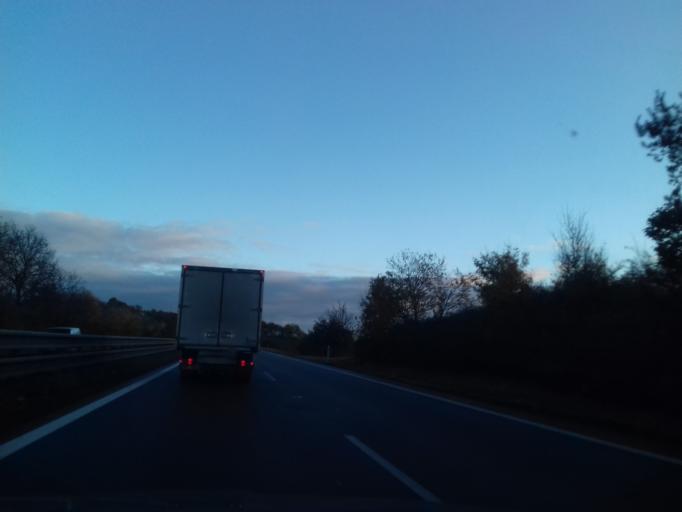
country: CZ
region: South Moravian
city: Pustimer
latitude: 49.3439
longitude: 17.0669
